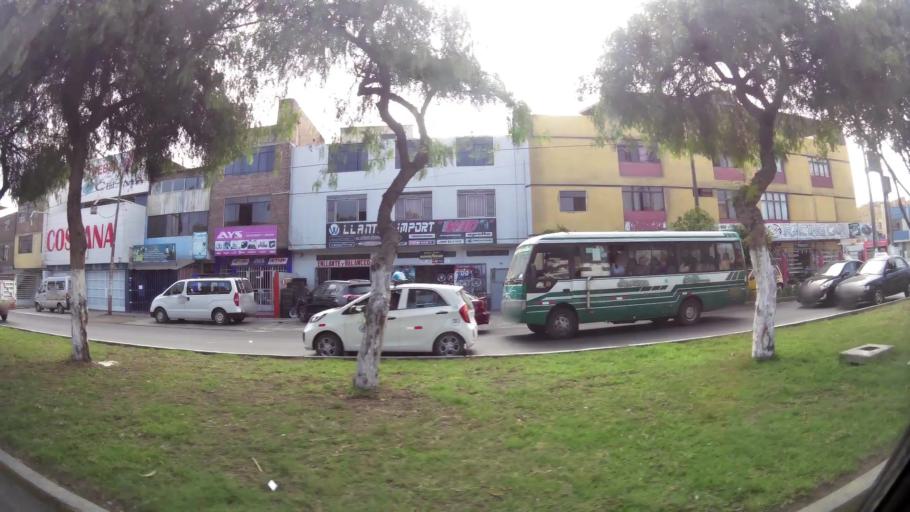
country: PE
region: La Libertad
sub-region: Provincia de Trujillo
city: Trujillo
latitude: -8.1073
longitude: -79.0115
